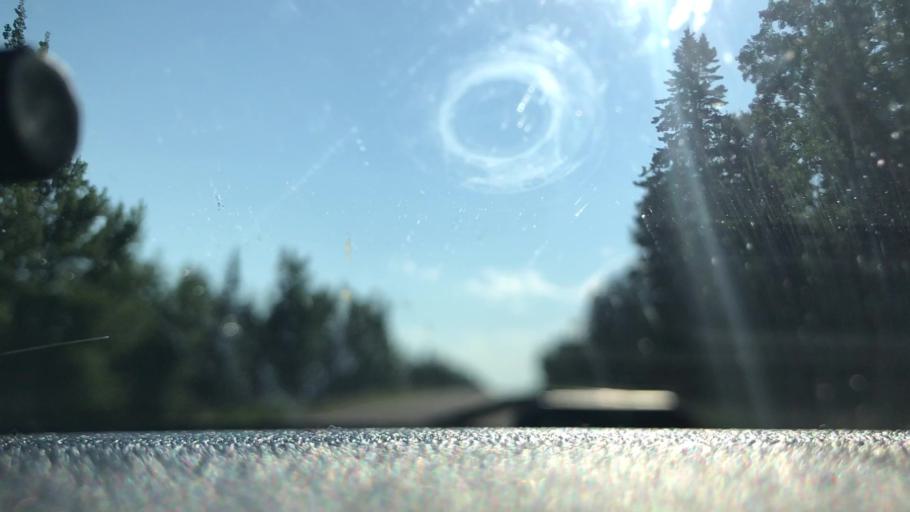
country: US
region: Minnesota
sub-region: Cook County
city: Grand Marais
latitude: 47.8284
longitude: -90.0015
